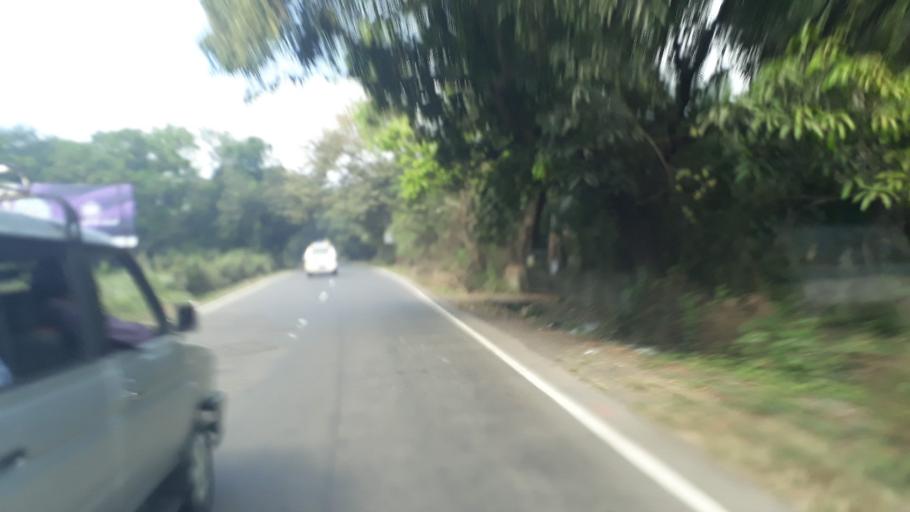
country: IN
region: Maharashtra
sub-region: Raigarh
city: Alibag
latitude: 18.6944
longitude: 72.9623
